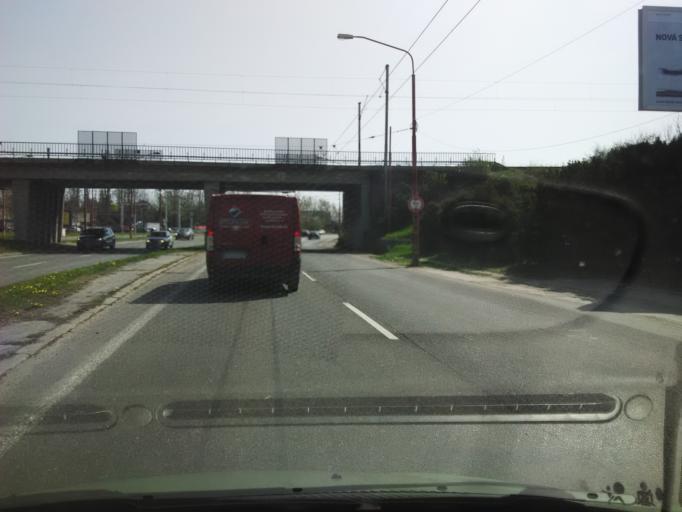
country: SK
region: Bratislavsky
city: Bratislava
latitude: 48.1443
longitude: 17.1881
